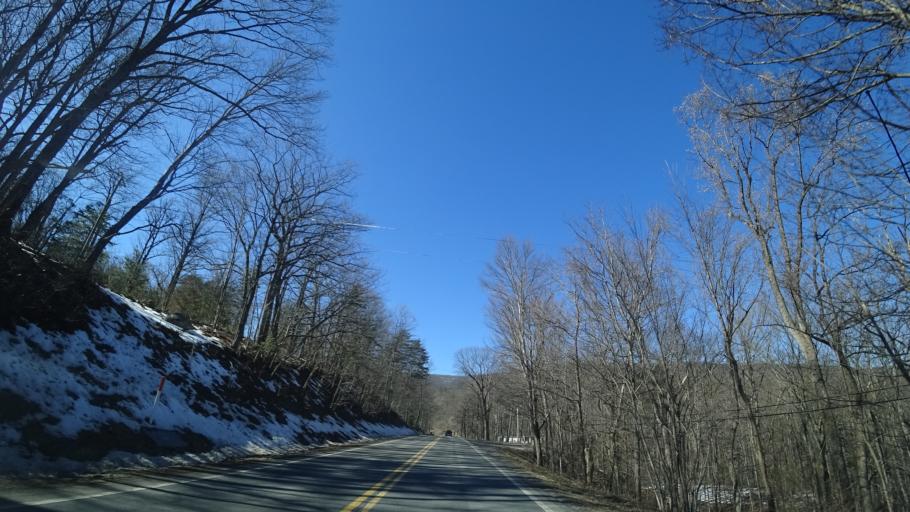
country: US
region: Virginia
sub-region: Frederick County
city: Shawnee Land
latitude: 39.0967
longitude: -78.4477
